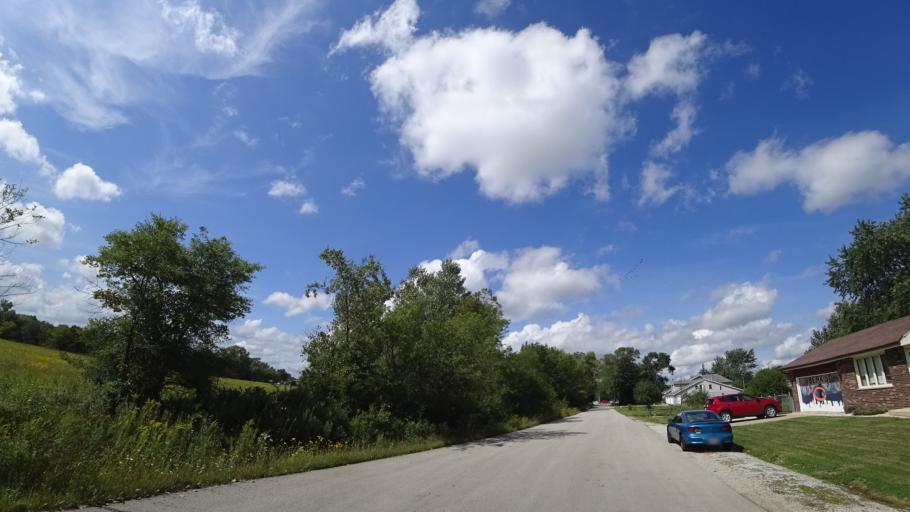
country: US
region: Illinois
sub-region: Cook County
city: Tinley Park
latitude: 41.5625
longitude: -87.7719
